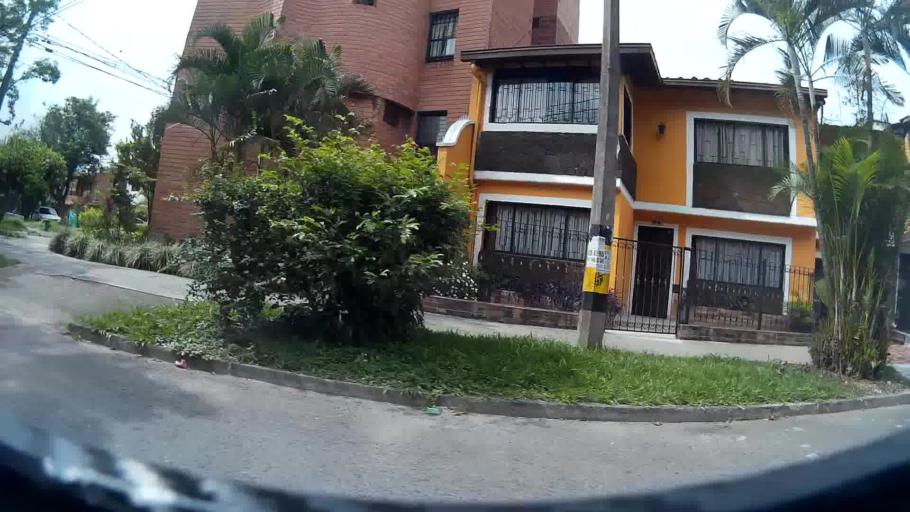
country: CO
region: Antioquia
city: Medellin
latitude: 6.2585
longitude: -75.6030
